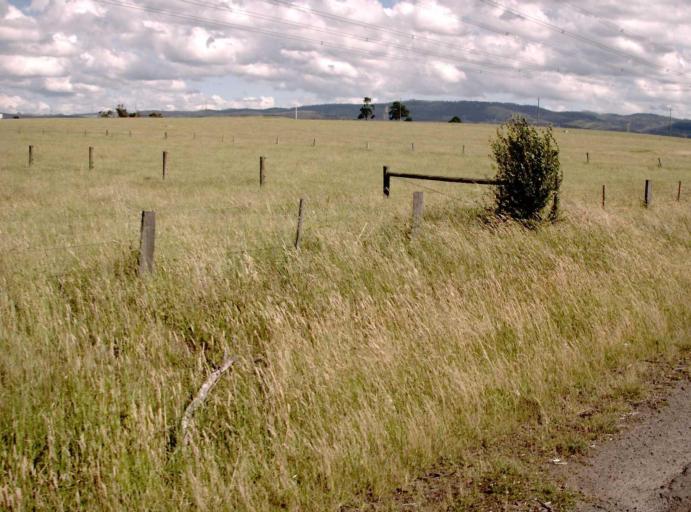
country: AU
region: Victoria
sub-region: Latrobe
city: Morwell
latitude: -38.2679
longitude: 146.4342
